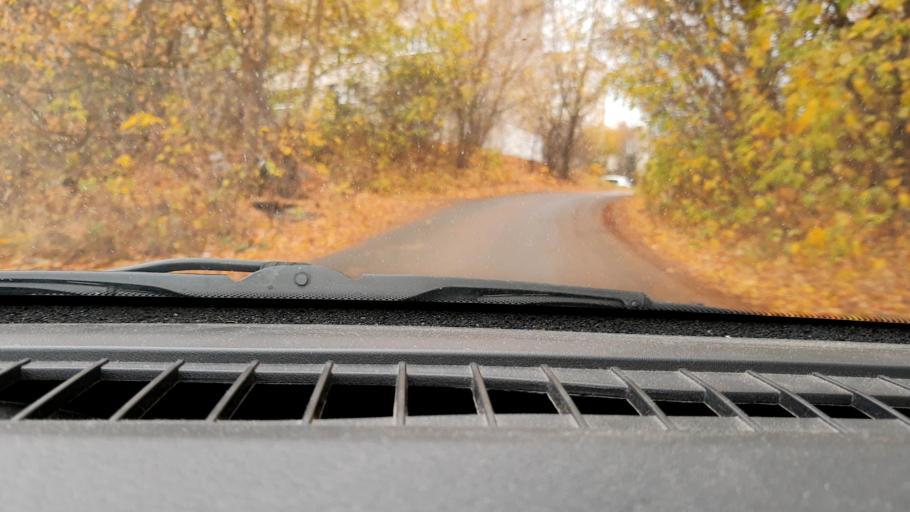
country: RU
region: Nizjnij Novgorod
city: Nizhniy Novgorod
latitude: 56.2299
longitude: 43.9578
